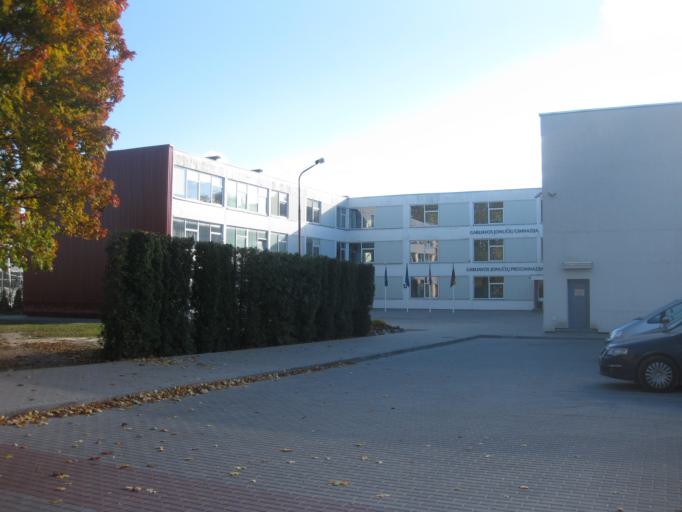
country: LT
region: Kauno apskritis
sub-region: Kauno rajonas
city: Garliava
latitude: 54.8350
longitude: 23.8802
